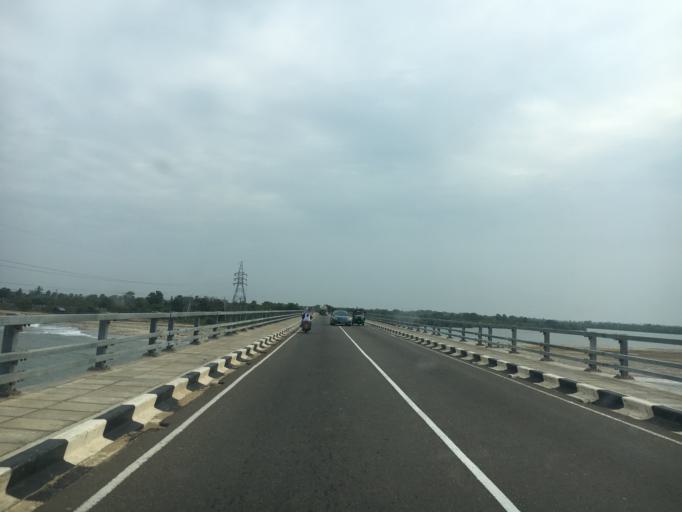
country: LK
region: Eastern Province
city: Trincomalee
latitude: 8.4710
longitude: 81.2023
